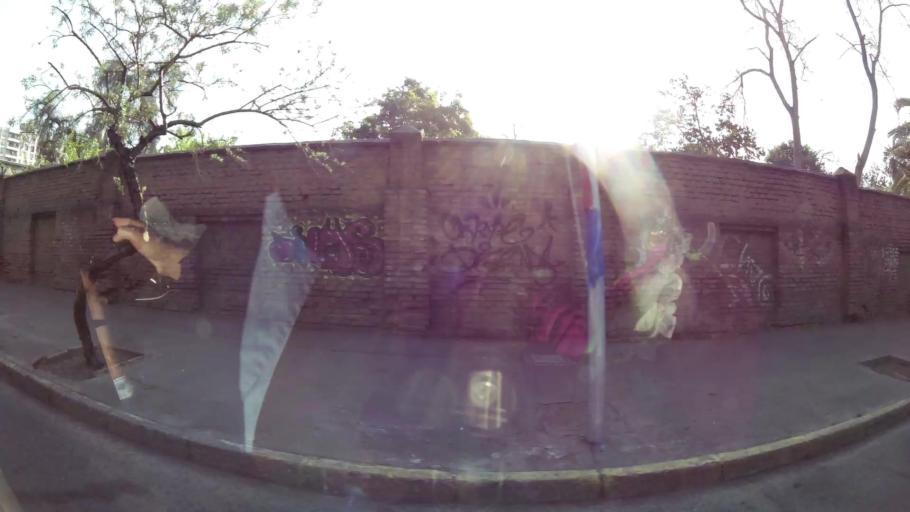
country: CL
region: Santiago Metropolitan
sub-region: Provincia de Santiago
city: Santiago
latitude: -33.4201
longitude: -70.6489
